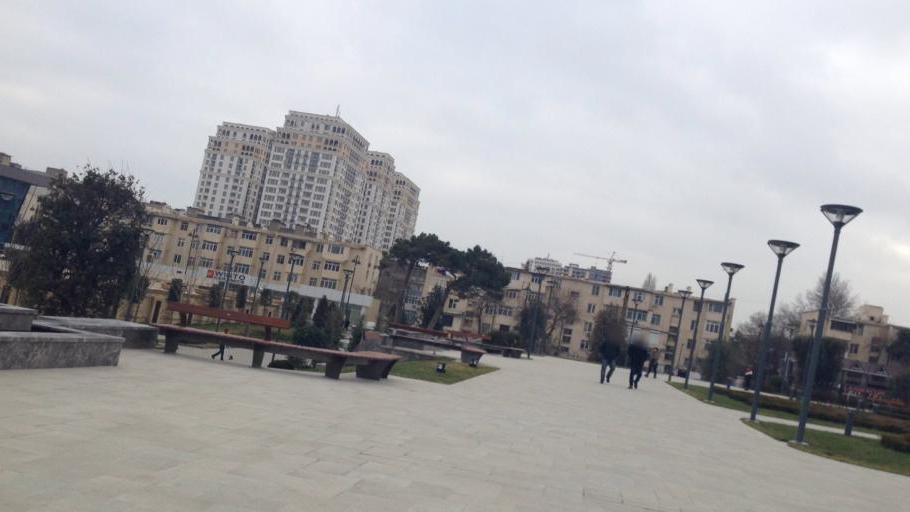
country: AZ
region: Baki
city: Badamdar
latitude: 40.3870
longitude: 49.8131
